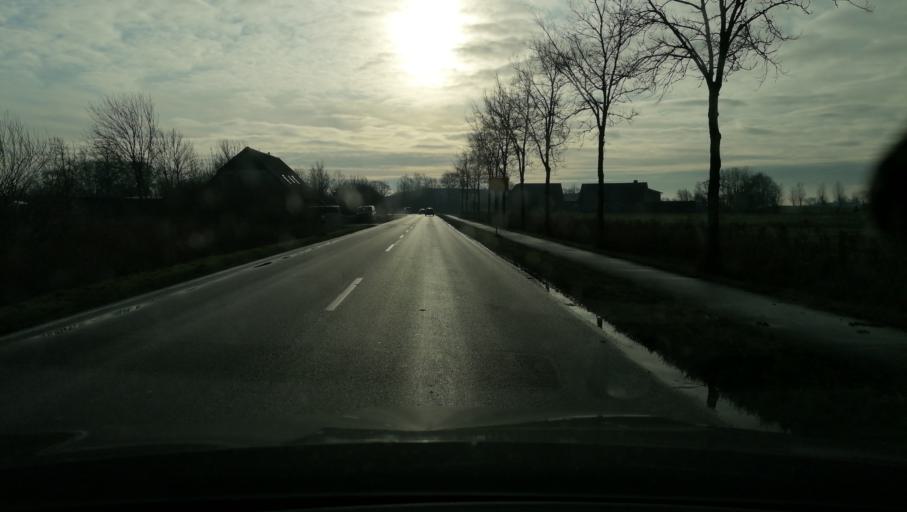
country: DE
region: Schleswig-Holstein
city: Epenwohrden
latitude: 54.1172
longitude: 9.0144
